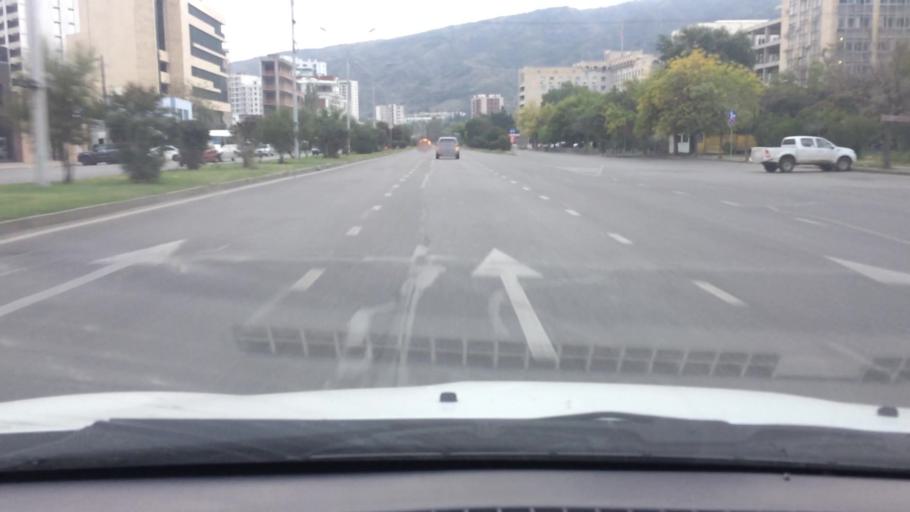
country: GE
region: T'bilisi
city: Tbilisi
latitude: 41.6801
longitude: 44.8270
